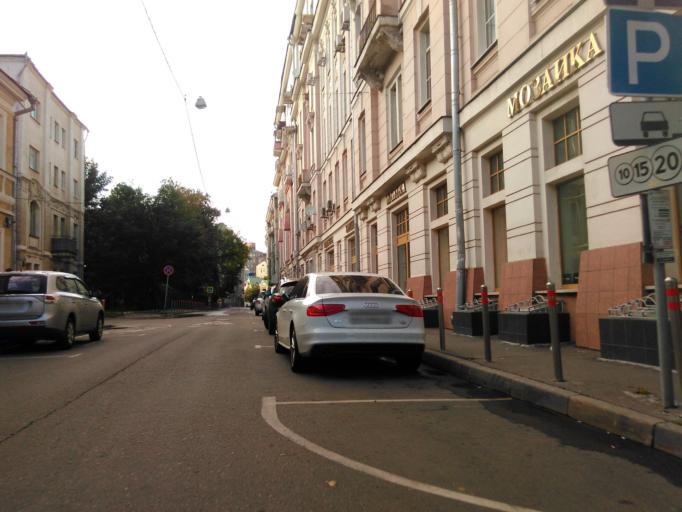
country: RU
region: Moscow
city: Taganskiy
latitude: 55.7583
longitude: 37.6526
